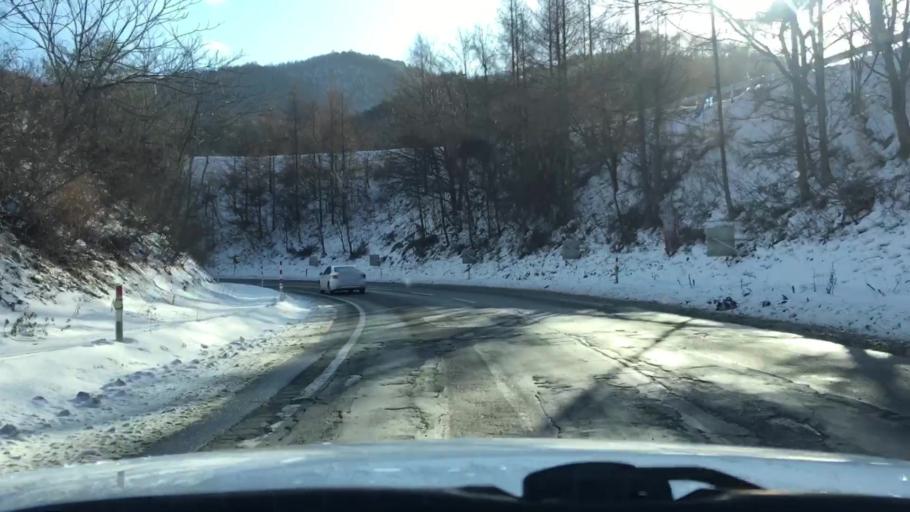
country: JP
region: Iwate
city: Morioka-shi
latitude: 39.6689
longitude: 141.3284
